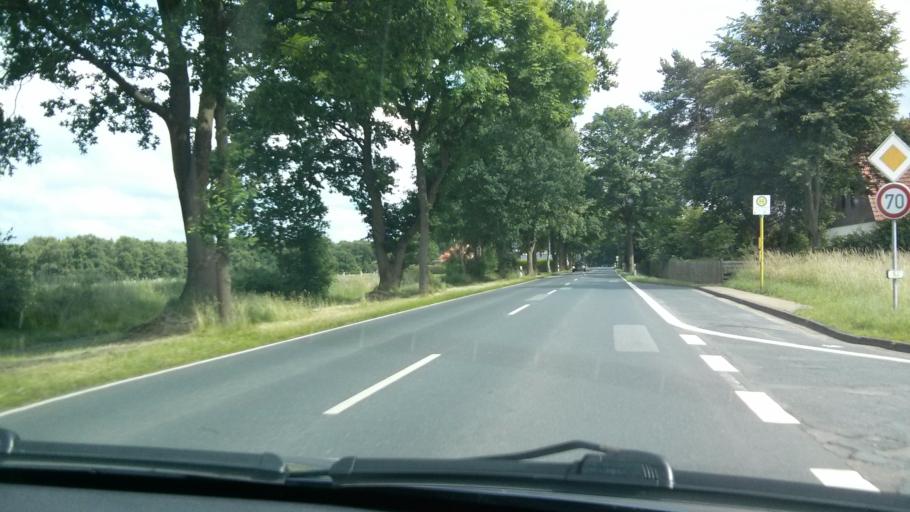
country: DE
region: Lower Saxony
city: Schiffdorf
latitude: 53.5225
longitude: 8.6682
